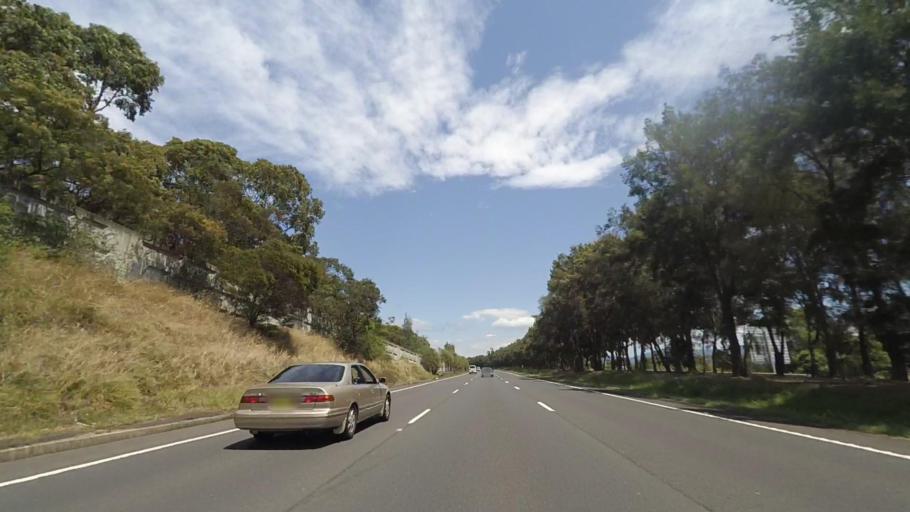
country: AU
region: New South Wales
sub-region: Wollongong
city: Berkeley
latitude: -34.4654
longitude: 150.8451
